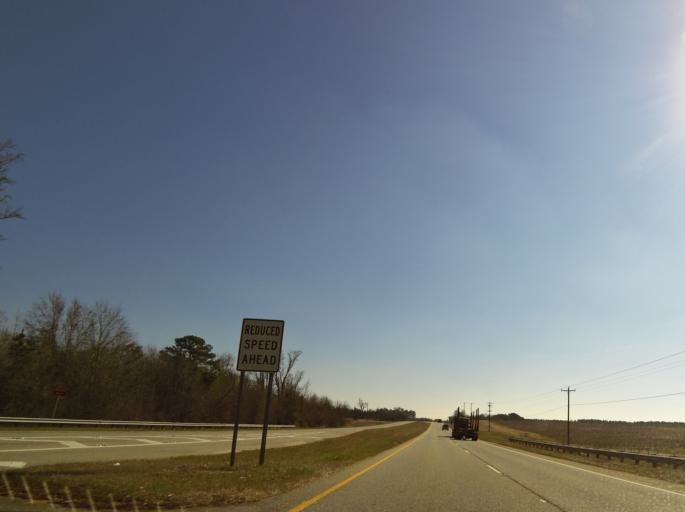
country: US
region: Georgia
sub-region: Pulaski County
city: Hawkinsville
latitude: 32.3114
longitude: -83.5175
